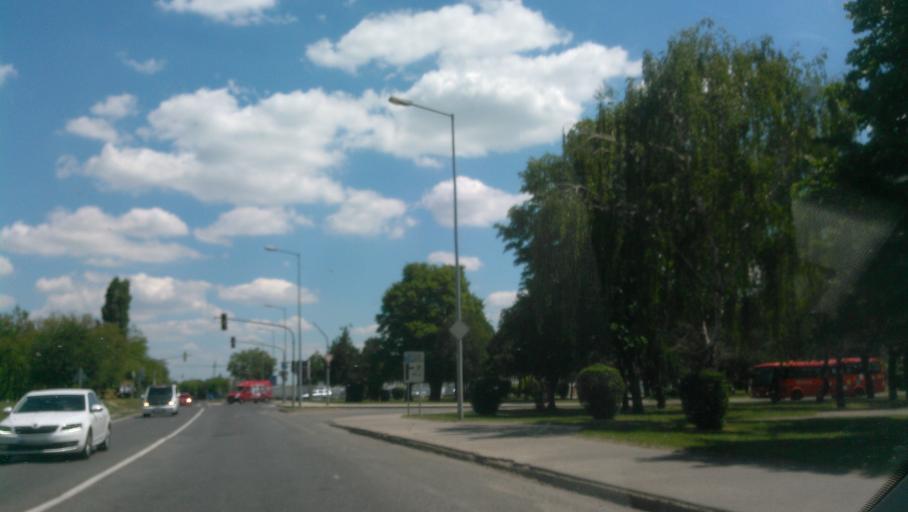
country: SK
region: Bratislavsky
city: Bratislava
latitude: 48.1295
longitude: 17.1757
